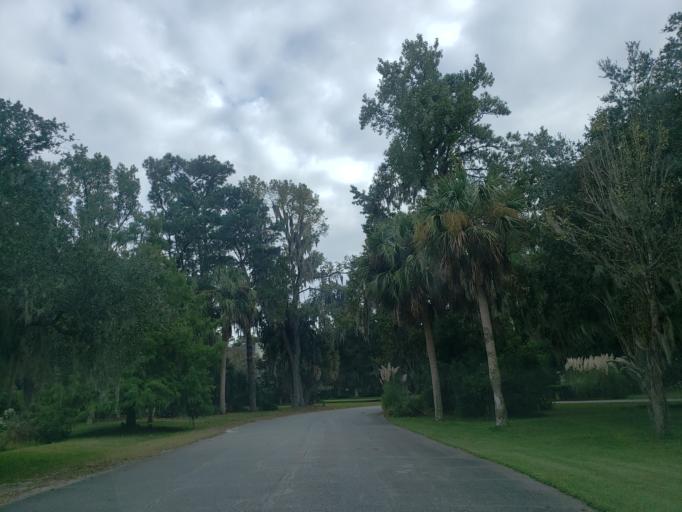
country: US
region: Georgia
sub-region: Chatham County
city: Montgomery
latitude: 31.9510
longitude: -81.1241
